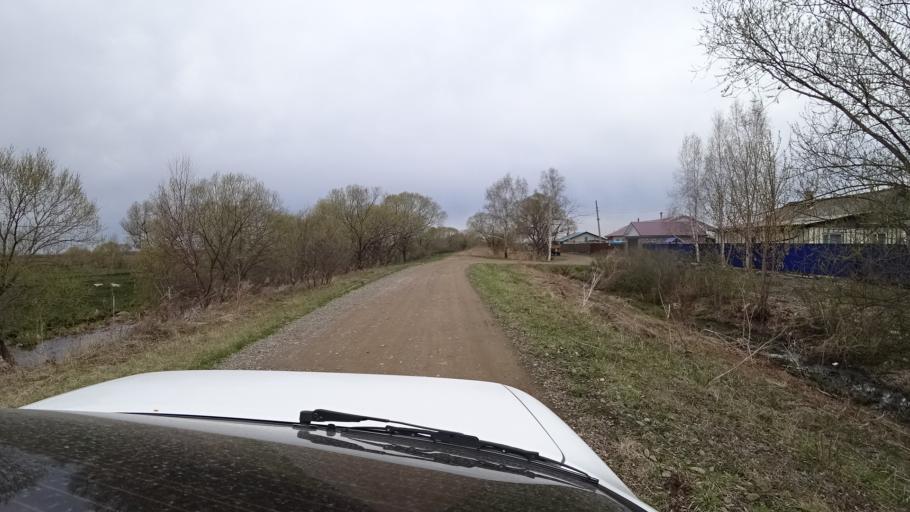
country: RU
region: Primorskiy
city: Dal'nerechensk
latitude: 45.9759
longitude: 133.7517
